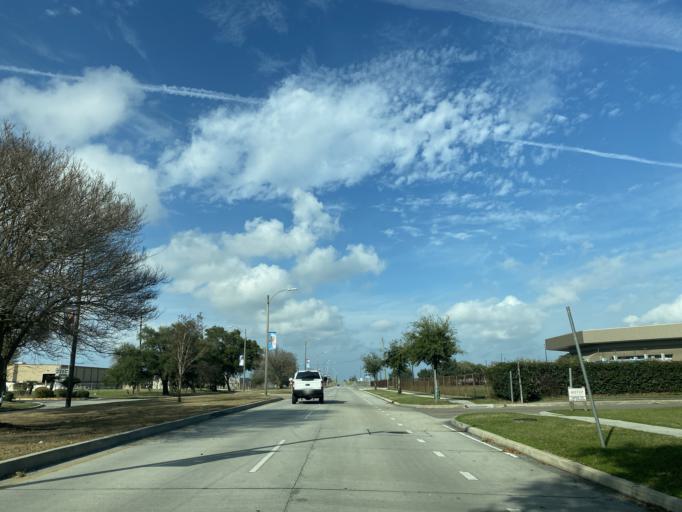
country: US
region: Louisiana
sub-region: Orleans Parish
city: New Orleans
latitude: 30.0275
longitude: -90.0522
